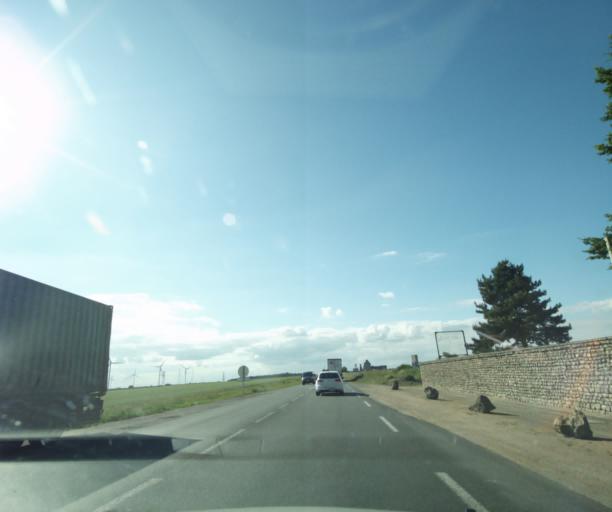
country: FR
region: Centre
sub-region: Departement d'Eure-et-Loir
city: Voves
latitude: 48.3160
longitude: 1.6763
